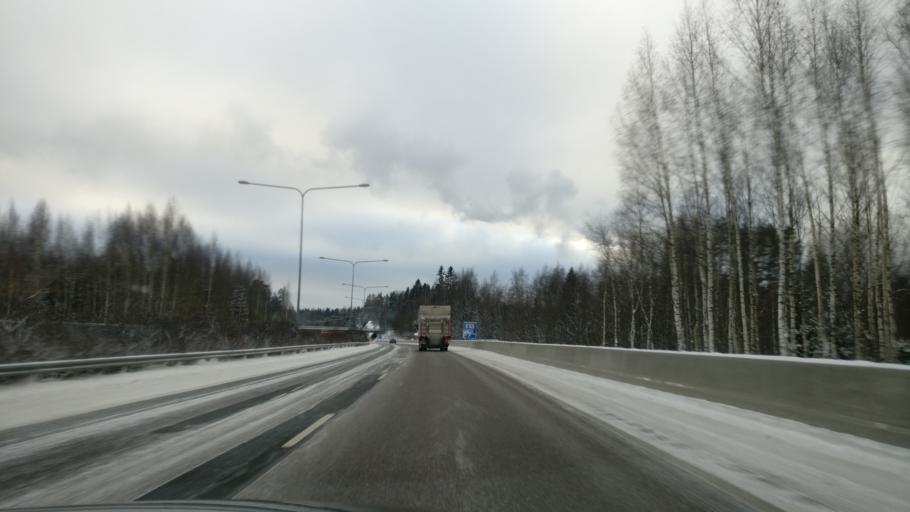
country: FI
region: Paijanne Tavastia
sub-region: Lahti
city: Lahti
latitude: 60.9910
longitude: 25.7493
